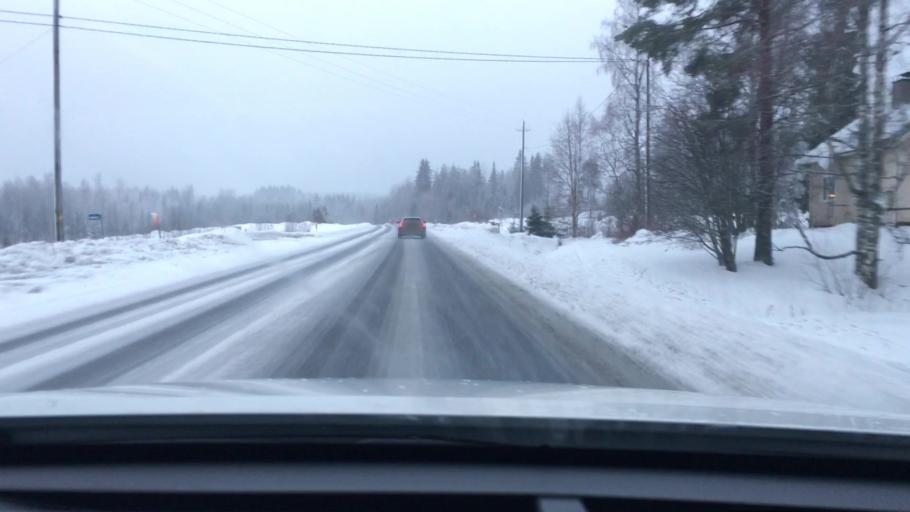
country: FI
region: Northern Savo
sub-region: Ylae-Savo
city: Sonkajaervi
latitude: 63.7596
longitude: 27.3997
